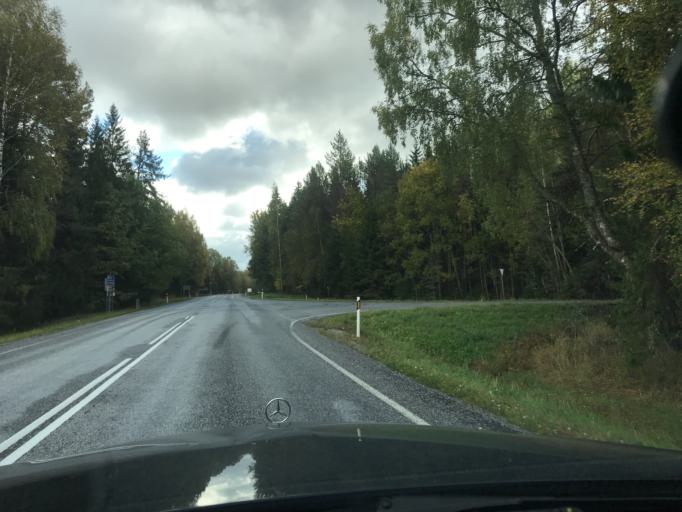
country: EE
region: Vorumaa
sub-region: Voru linn
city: Voru
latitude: 57.7279
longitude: 27.3098
